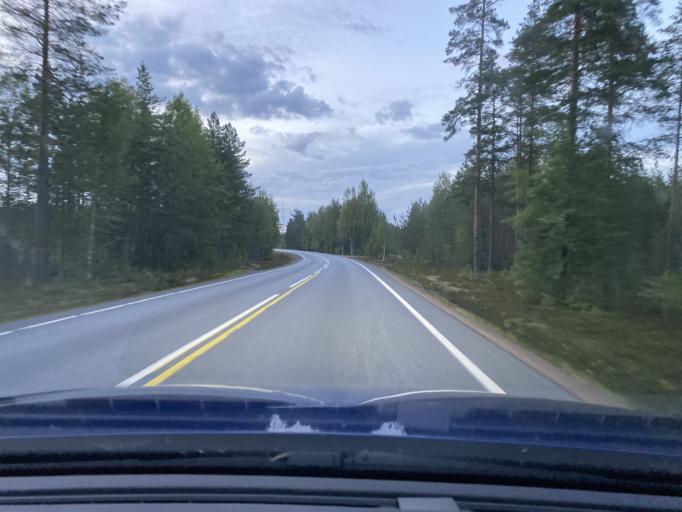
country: FI
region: Southern Ostrobothnia
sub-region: Suupohja
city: Kauhajoki
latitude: 62.2353
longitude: 22.2723
